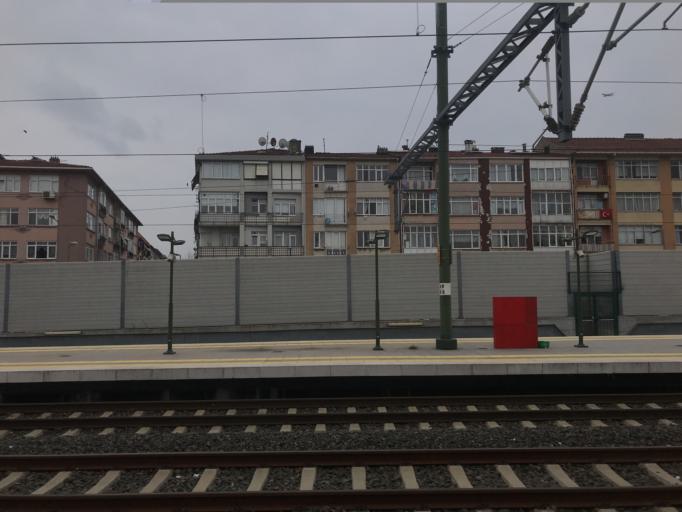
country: TR
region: Istanbul
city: Pendik
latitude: 40.8804
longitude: 29.2343
